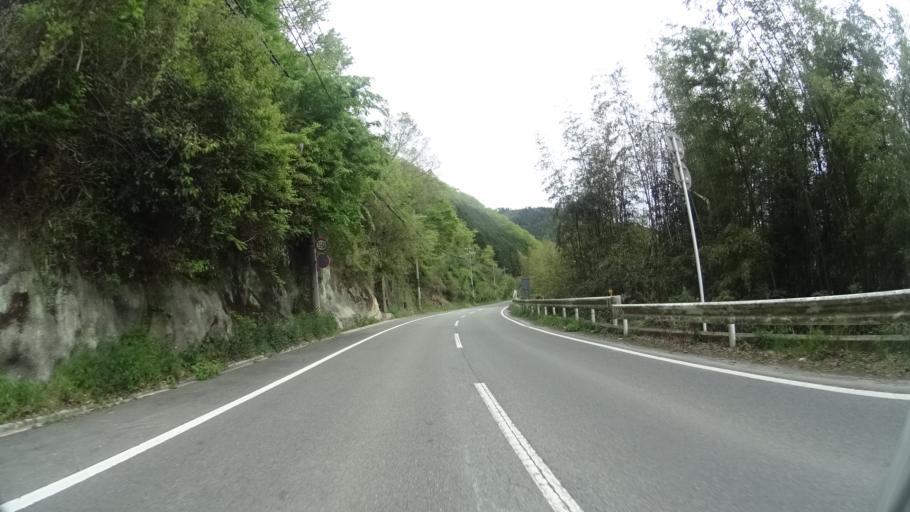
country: JP
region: Kyoto
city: Kameoka
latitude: 35.1189
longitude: 135.5142
